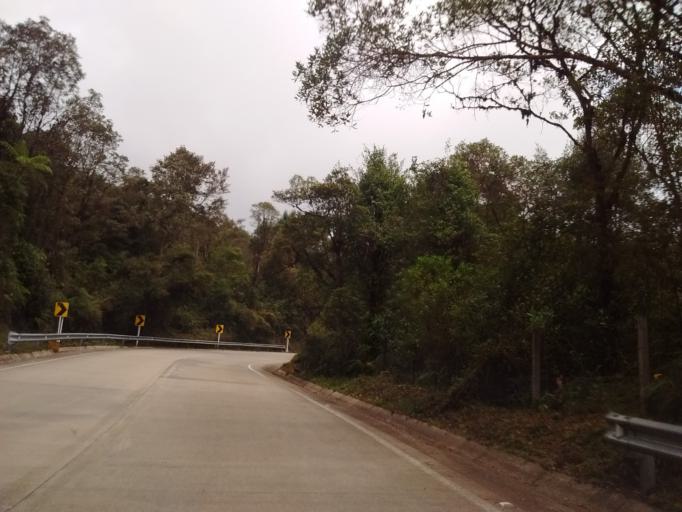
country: CO
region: Huila
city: Isnos
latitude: 2.0485
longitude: -76.3084
